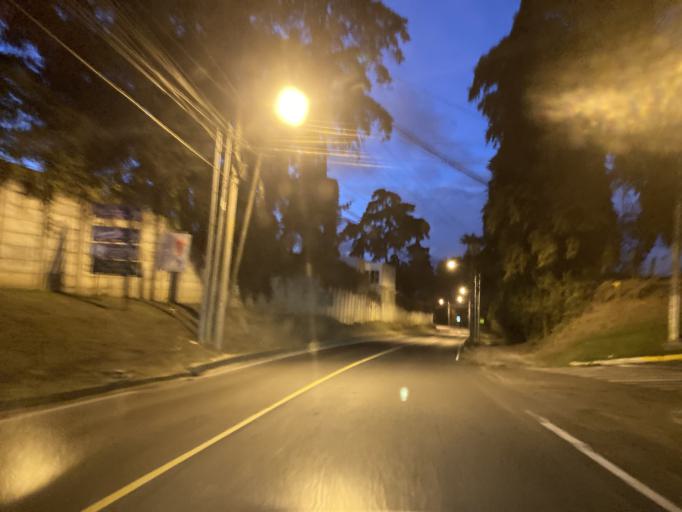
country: GT
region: Guatemala
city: Santa Catarina Pinula
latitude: 14.6029
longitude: -90.4675
